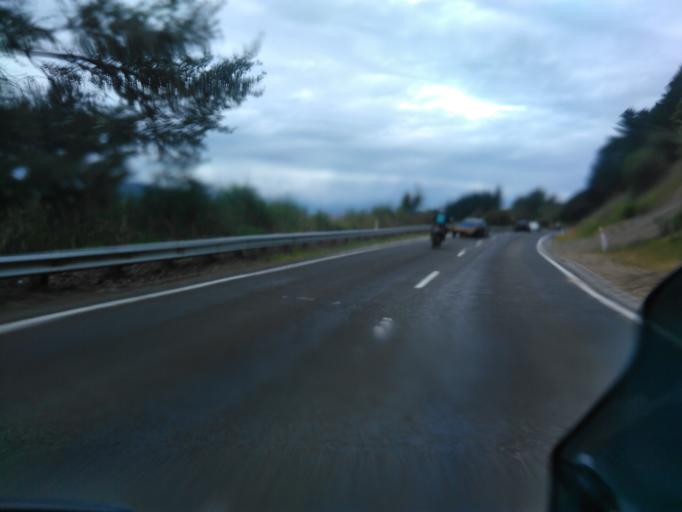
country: NZ
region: Gisborne
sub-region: Gisborne District
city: Gisborne
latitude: -38.4762
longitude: 177.6920
